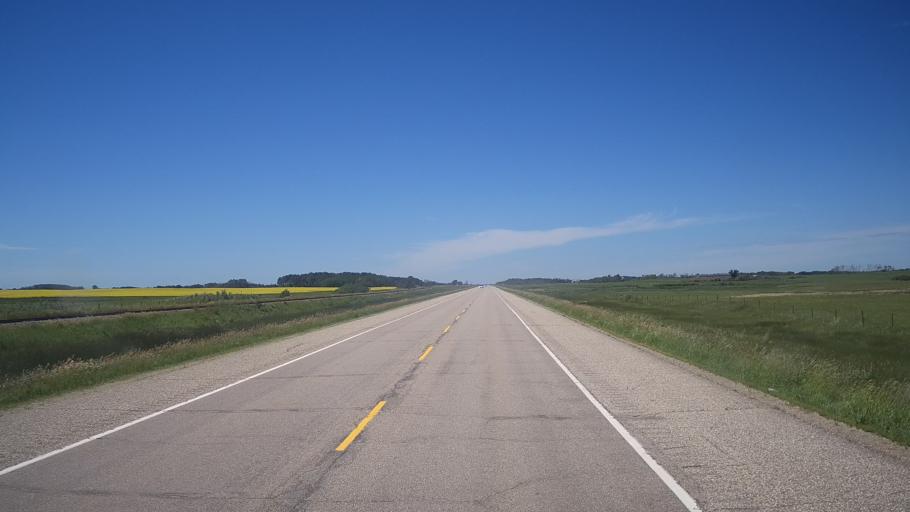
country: CA
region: Manitoba
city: Rivers
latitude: 50.4219
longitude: -100.4961
